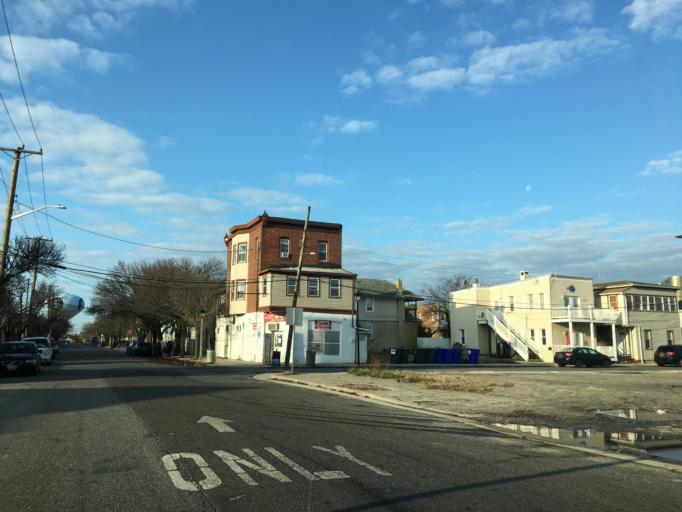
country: US
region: New Jersey
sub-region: Atlantic County
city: Atlantic City
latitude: 39.3721
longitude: -74.4205
